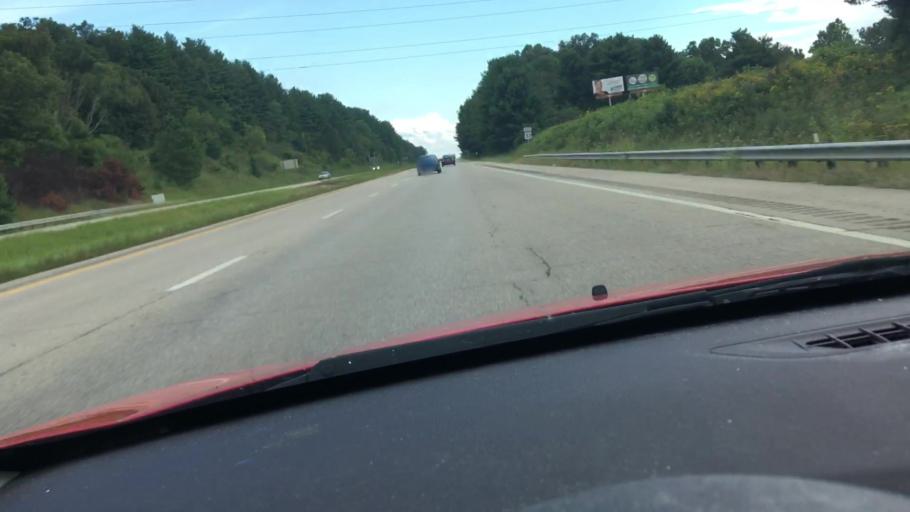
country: US
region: Ohio
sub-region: Athens County
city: The Plains
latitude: 39.3785
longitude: -82.1323
